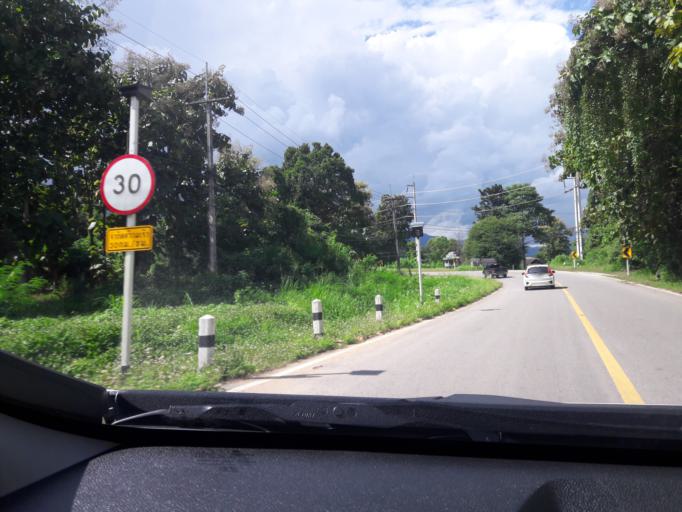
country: TH
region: Mae Hong Son
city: Mae Hi
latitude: 19.3137
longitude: 98.4501
